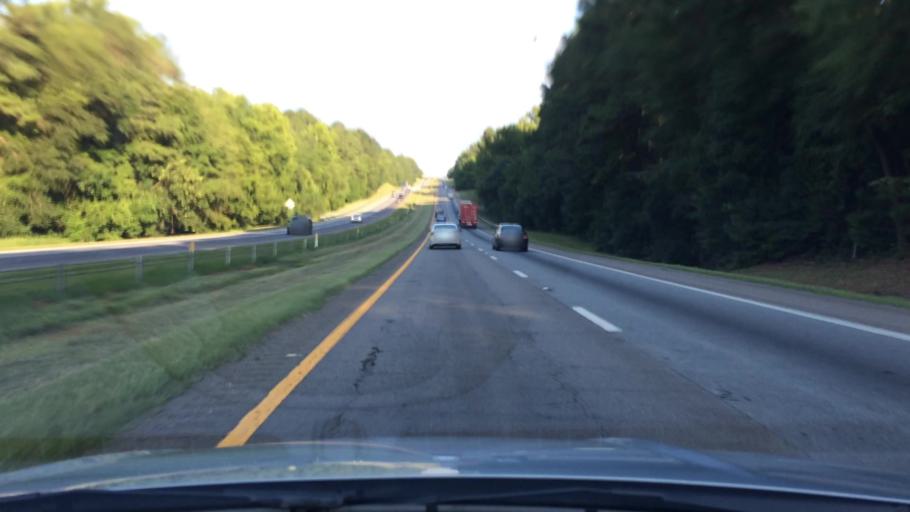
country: US
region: South Carolina
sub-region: Newberry County
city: Prosperity
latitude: 34.2593
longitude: -81.4980
